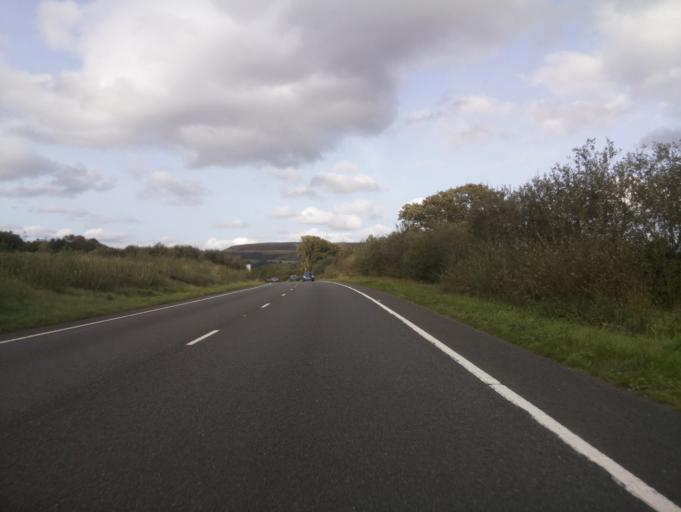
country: GB
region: Wales
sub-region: Rhondda Cynon Taf
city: Llantwit Fardre
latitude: 51.5638
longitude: -3.3052
